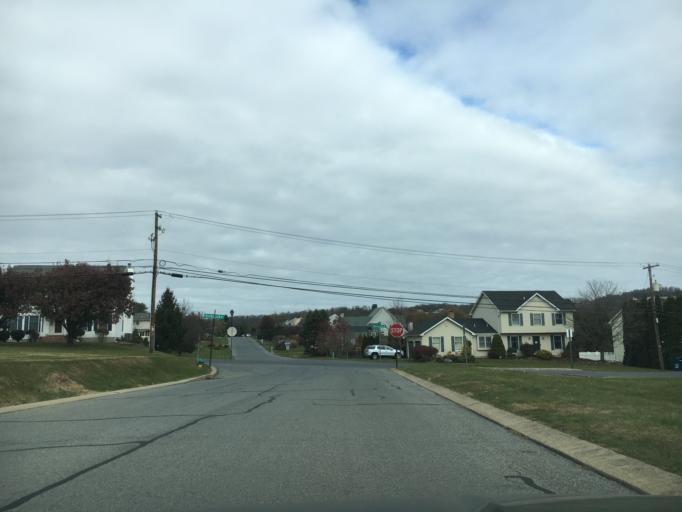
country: US
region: Pennsylvania
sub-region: Lehigh County
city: Laurys Station
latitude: 40.7232
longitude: -75.5339
